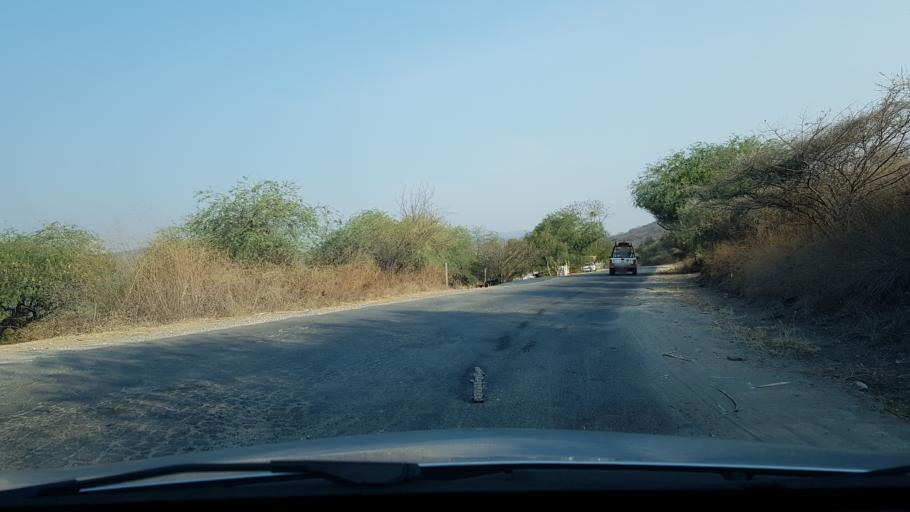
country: MX
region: Morelos
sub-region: Tlaltizapan de Zapata
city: Colonia Palo Prieto (Chipitongo)
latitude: 18.6921
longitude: -99.0999
